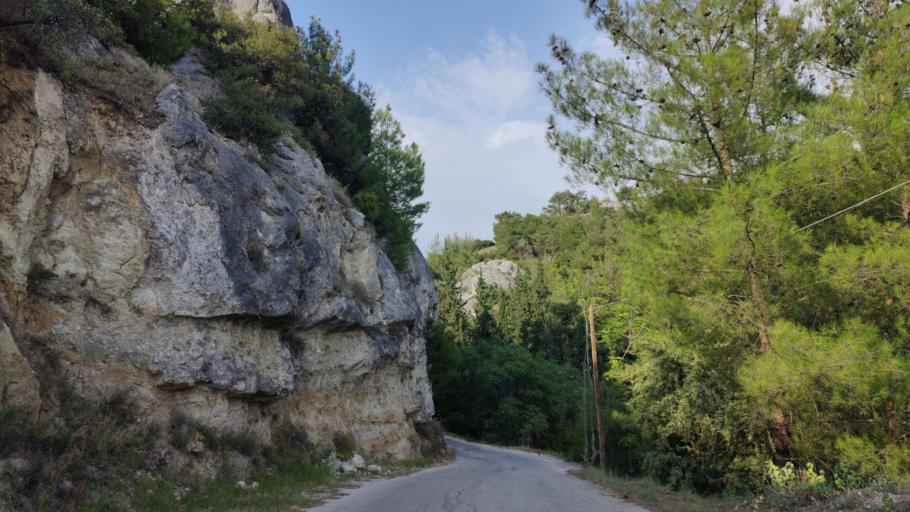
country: GR
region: Central Macedonia
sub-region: Nomos Serron
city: Sidirokastro
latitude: 41.2363
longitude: 23.4004
